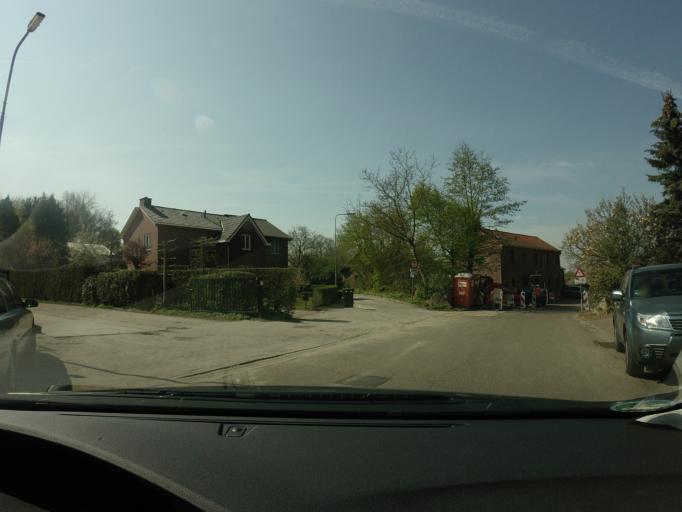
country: NL
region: Limburg
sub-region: Eijsden-Margraten
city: Margraten
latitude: 50.8292
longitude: 5.8115
